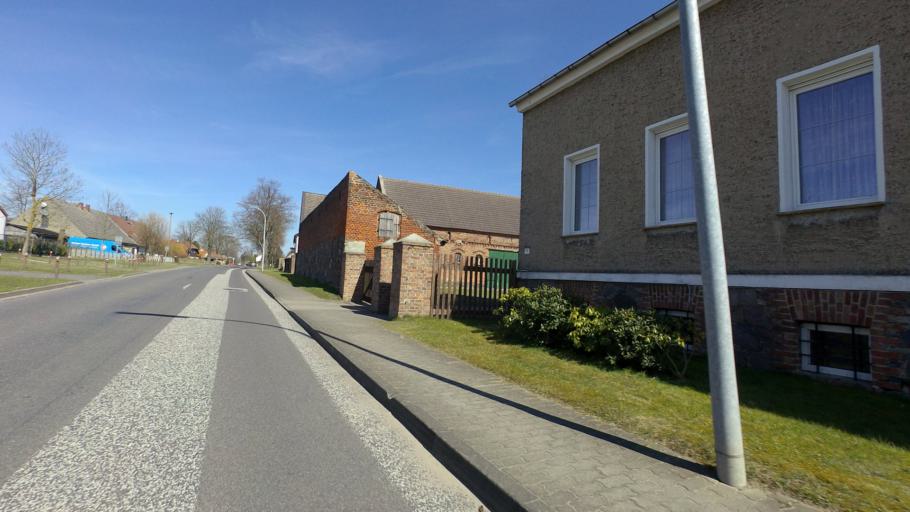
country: DE
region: Brandenburg
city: Furstenwalde
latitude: 52.4307
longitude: 14.0446
